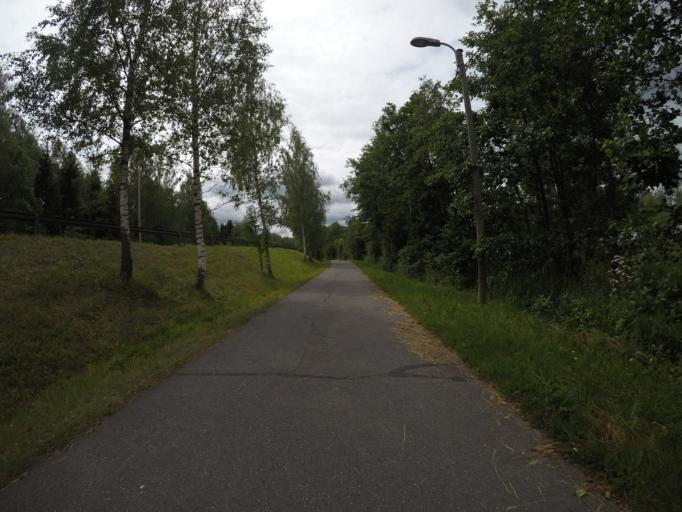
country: FI
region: Haeme
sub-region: Haemeenlinna
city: Haemeenlinna
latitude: 61.0009
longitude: 24.5009
